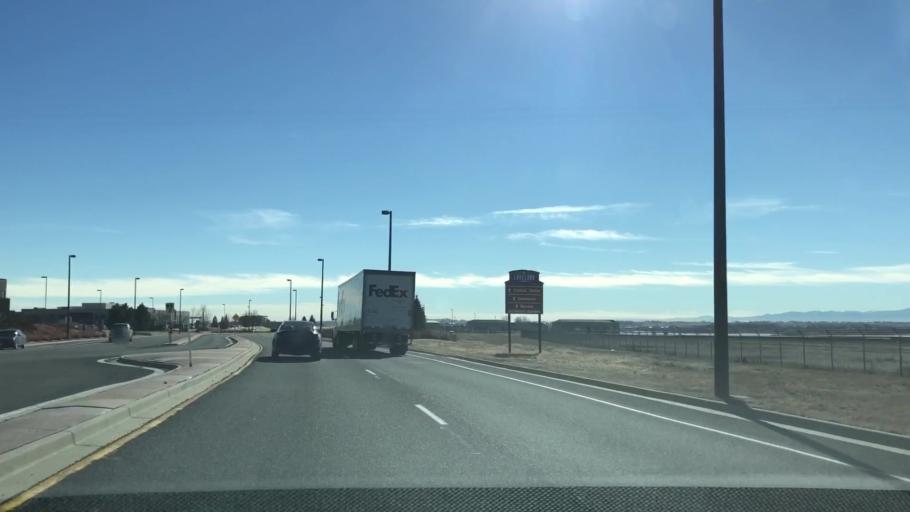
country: US
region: Colorado
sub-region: Larimer County
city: Loveland
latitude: 40.4270
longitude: -105.0004
